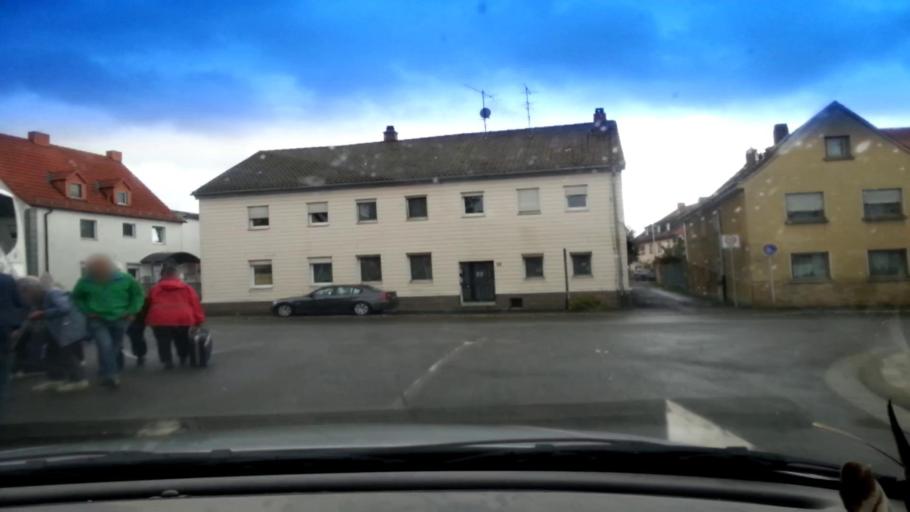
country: DE
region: Bavaria
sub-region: Upper Franconia
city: Hallstadt
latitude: 49.9306
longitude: 10.8785
